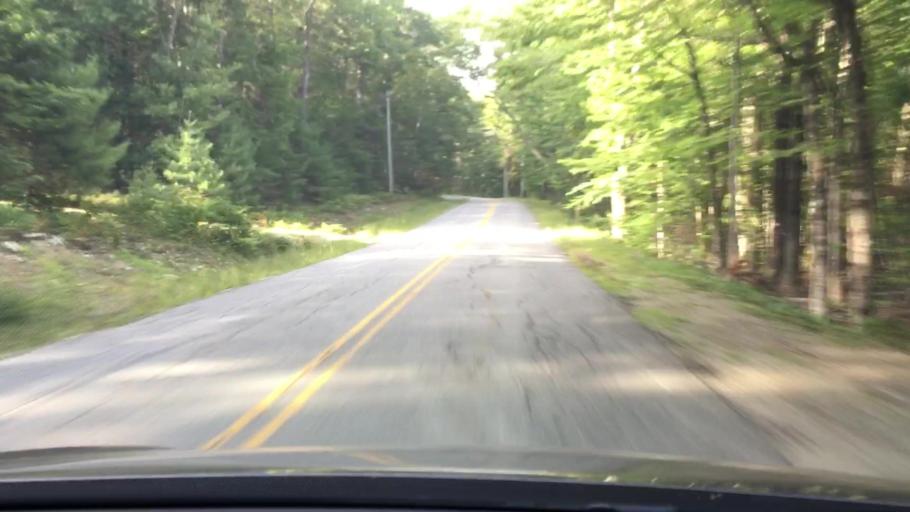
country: US
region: Maine
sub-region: Hancock County
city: Orland
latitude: 44.5291
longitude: -68.7635
